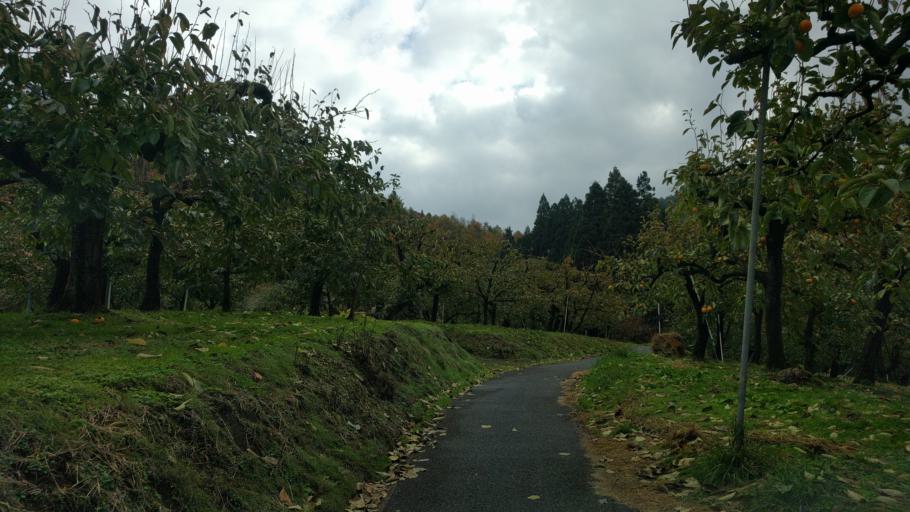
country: JP
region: Fukushima
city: Kitakata
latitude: 37.4590
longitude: 139.9378
